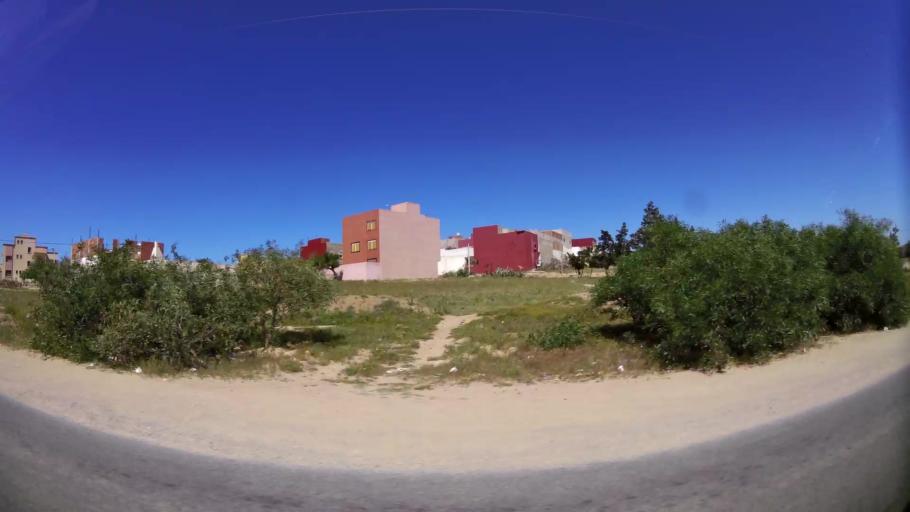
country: MA
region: Oriental
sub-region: Berkane-Taourirt
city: Madagh
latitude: 35.1272
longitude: -2.4236
